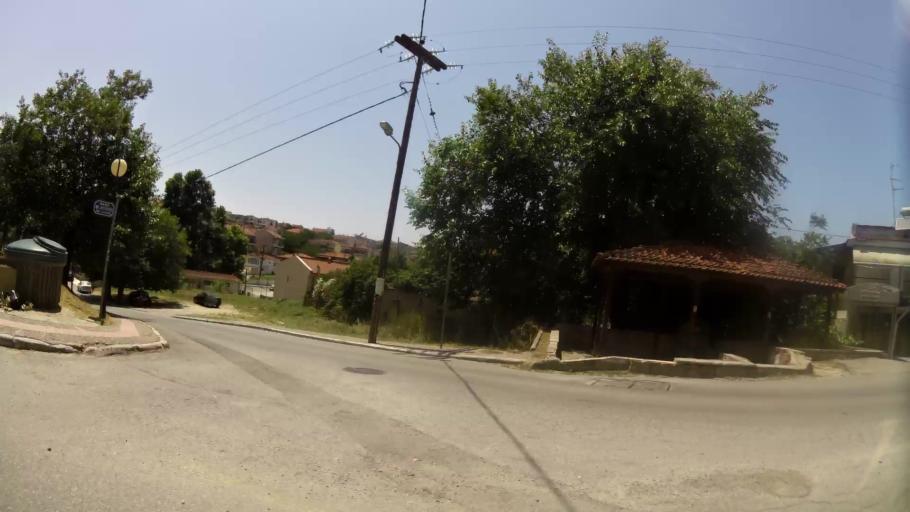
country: GR
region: Central Macedonia
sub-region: Nomos Thessalonikis
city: Trilofos
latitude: 40.4689
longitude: 22.9695
